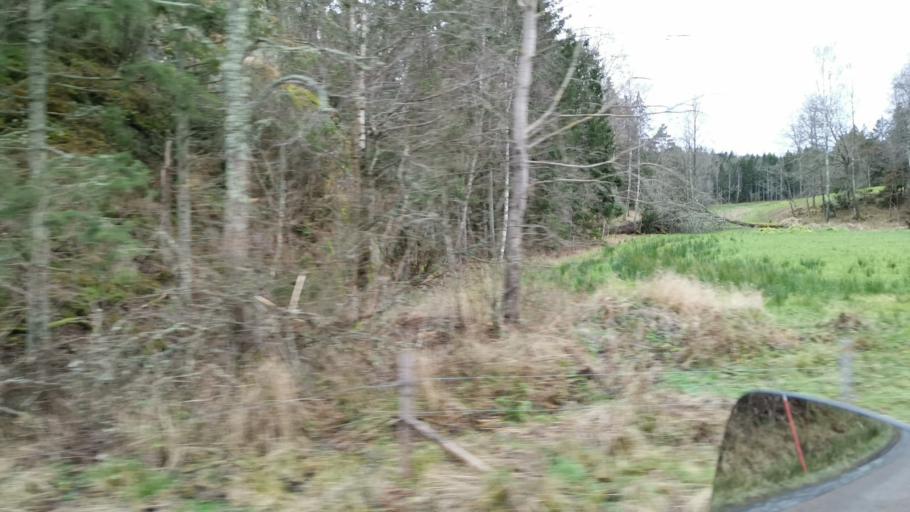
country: SE
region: Vaestra Goetaland
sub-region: Orust
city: Henan
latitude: 58.2101
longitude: 11.7318
